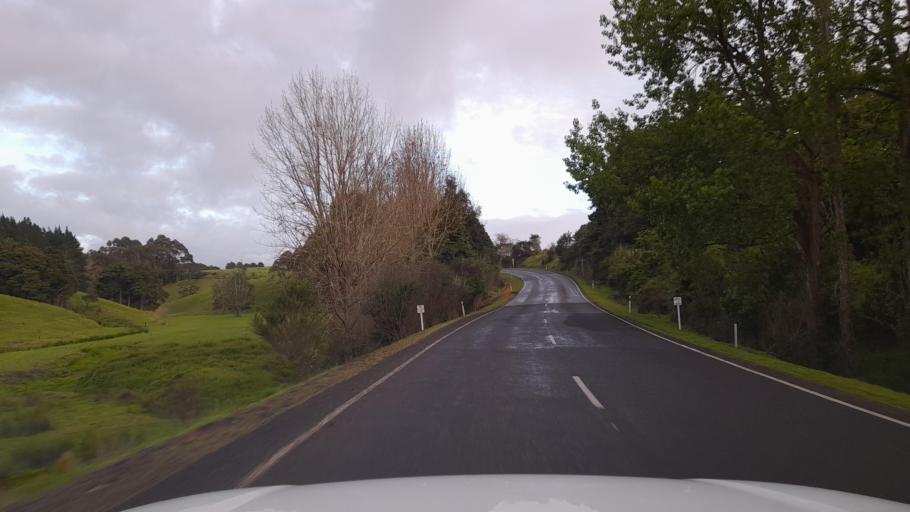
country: NZ
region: Northland
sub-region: Kaipara District
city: Dargaville
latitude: -35.6982
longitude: 173.9114
